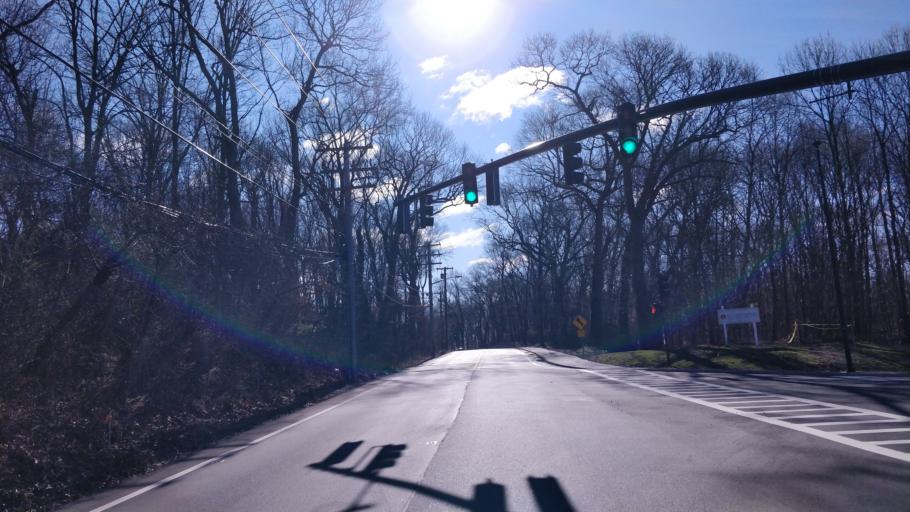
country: US
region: New York
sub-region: Suffolk County
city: Stony Brook
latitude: 40.9024
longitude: -73.1317
